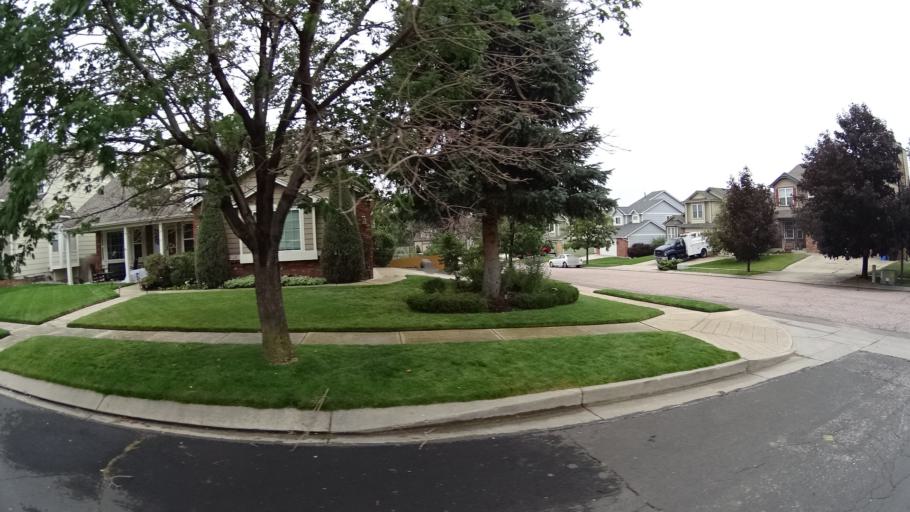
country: US
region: Colorado
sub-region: El Paso County
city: Cimarron Hills
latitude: 38.9319
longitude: -104.7559
